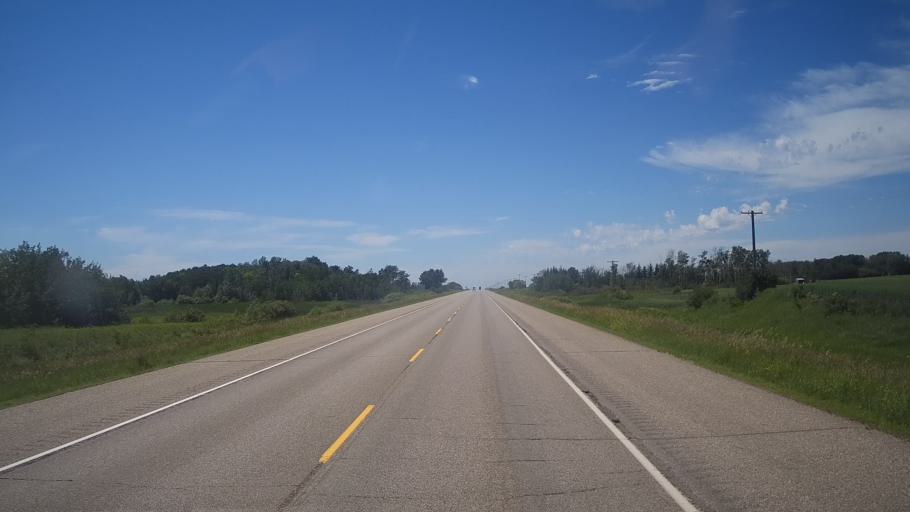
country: CA
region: Saskatchewan
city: Langenburg
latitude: 50.7714
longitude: -101.3056
